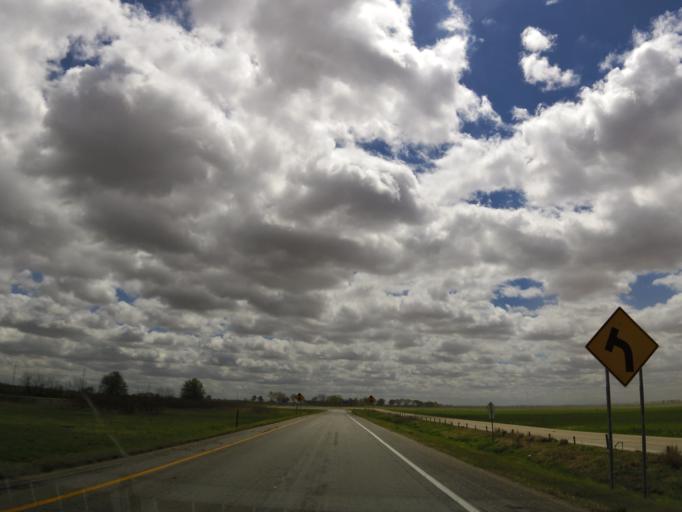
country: US
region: Arkansas
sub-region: Poinsett County
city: Trumann
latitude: 35.6311
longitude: -90.5023
